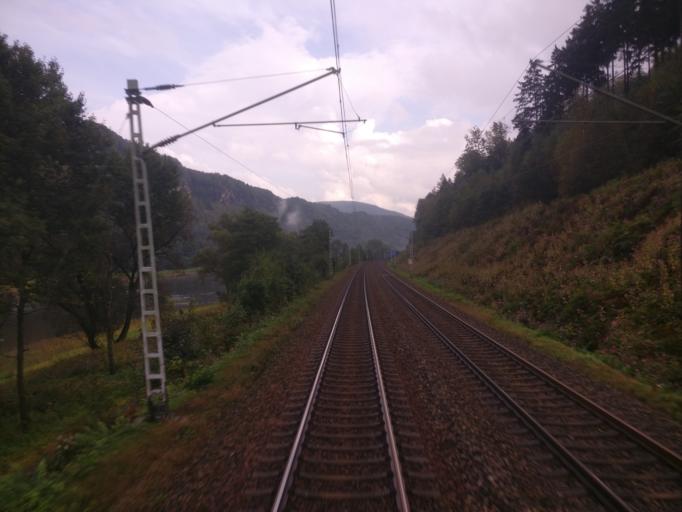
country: DE
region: Saxony
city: Bad Schandau
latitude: 50.9053
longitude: 14.1996
